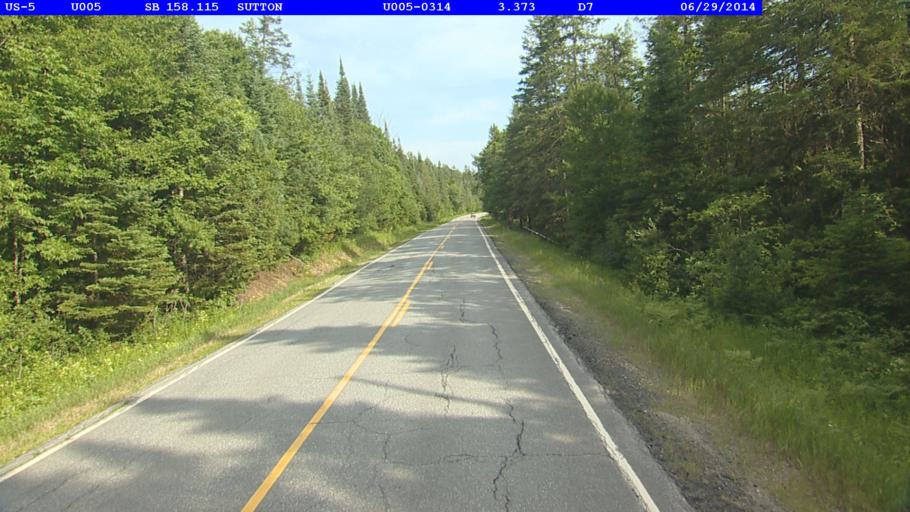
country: US
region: Vermont
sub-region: Caledonia County
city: Lyndonville
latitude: 44.6746
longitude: -72.0294
